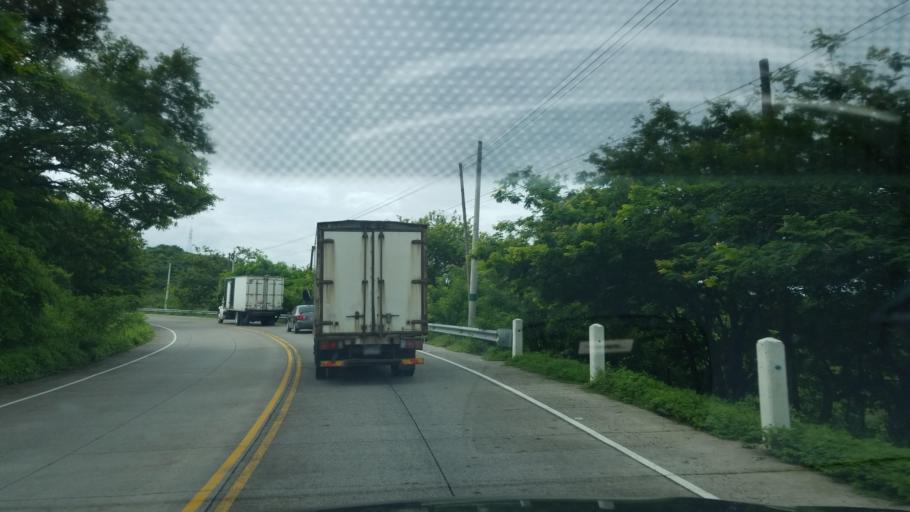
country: HN
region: Francisco Morazan
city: El Porvenir
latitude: 13.6805
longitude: -87.3552
